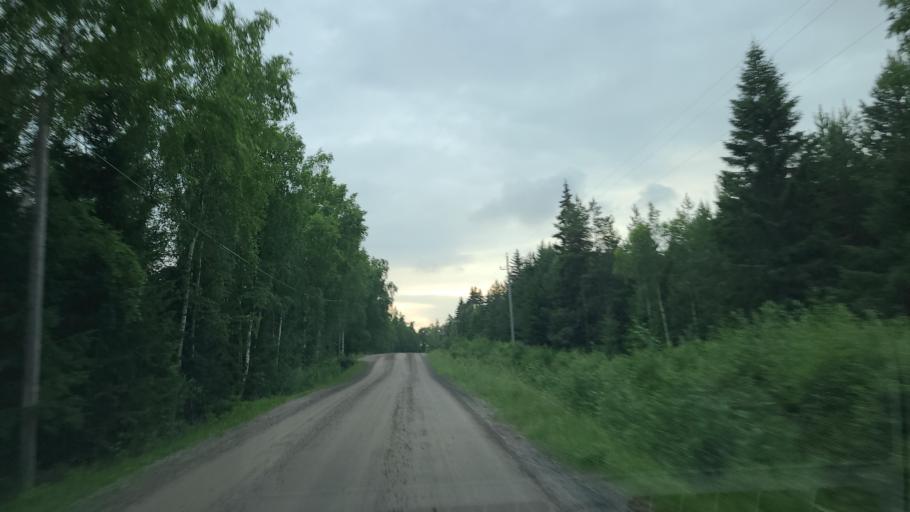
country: FI
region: Ostrobothnia
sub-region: Vaasa
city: Replot
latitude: 63.3207
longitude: 21.1448
